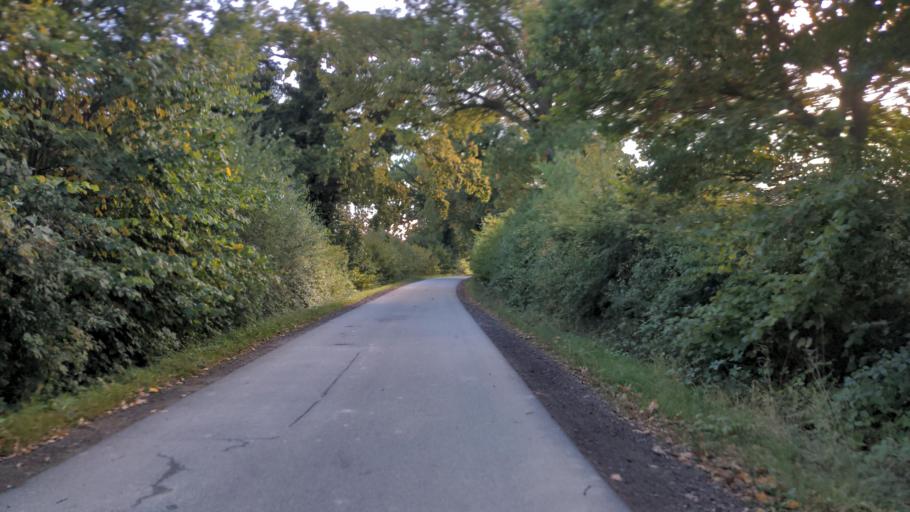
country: DE
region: Schleswig-Holstein
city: Manhagen
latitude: 54.1908
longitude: 10.9107
